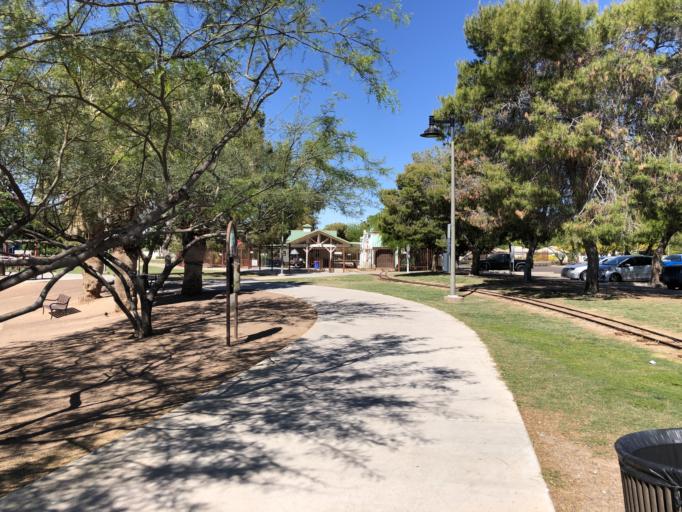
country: US
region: Arizona
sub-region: Maricopa County
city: Guadalupe
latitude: 33.3141
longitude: -111.9198
